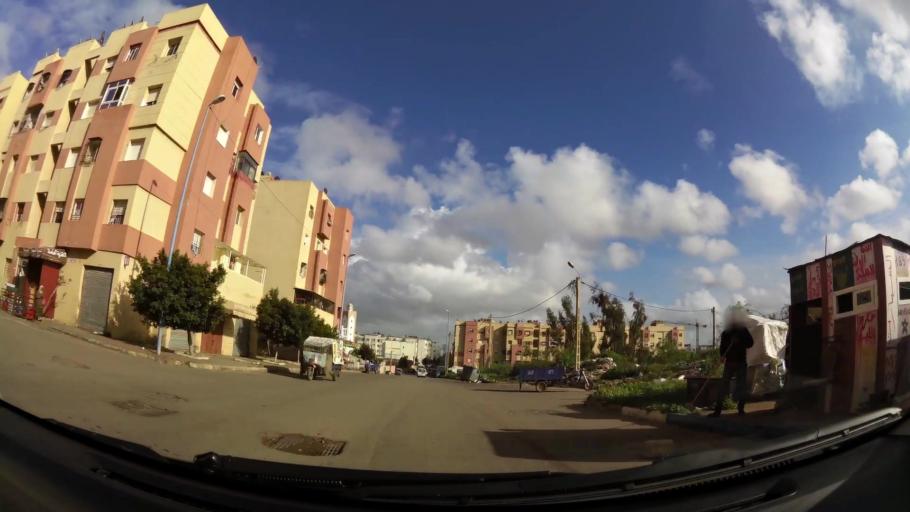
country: MA
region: Grand Casablanca
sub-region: Casablanca
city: Casablanca
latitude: 33.5501
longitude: -7.7054
